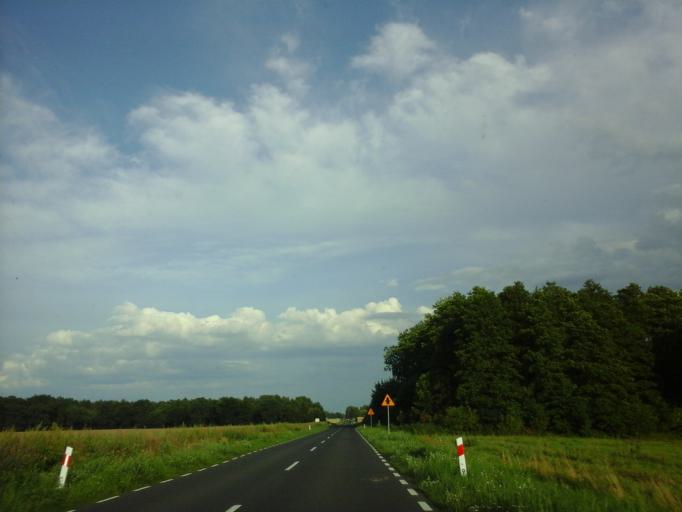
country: PL
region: West Pomeranian Voivodeship
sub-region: Powiat kamienski
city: Swierzno
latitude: 53.8897
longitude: 14.8767
